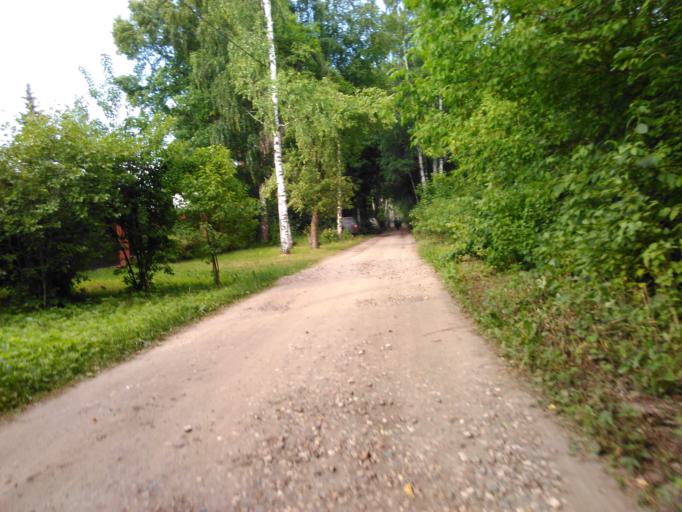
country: RU
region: Moskovskaya
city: Vishnyakovskiye Dachi
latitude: 55.7638
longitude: 38.1436
